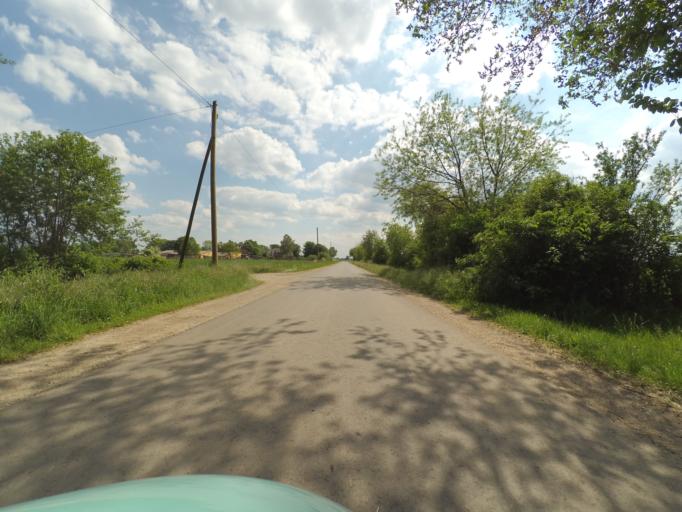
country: DE
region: Lower Saxony
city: Haenigsen
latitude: 52.5152
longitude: 10.0808
